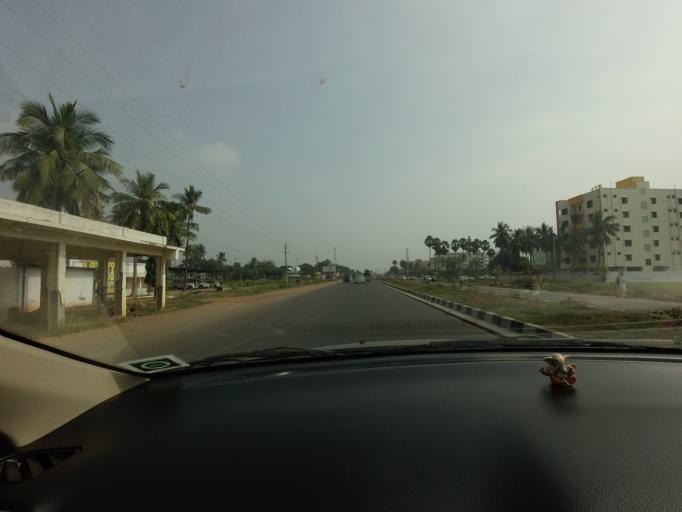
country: IN
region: Andhra Pradesh
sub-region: Krishna
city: Yanamalakuduru
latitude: 16.4692
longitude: 80.7254
